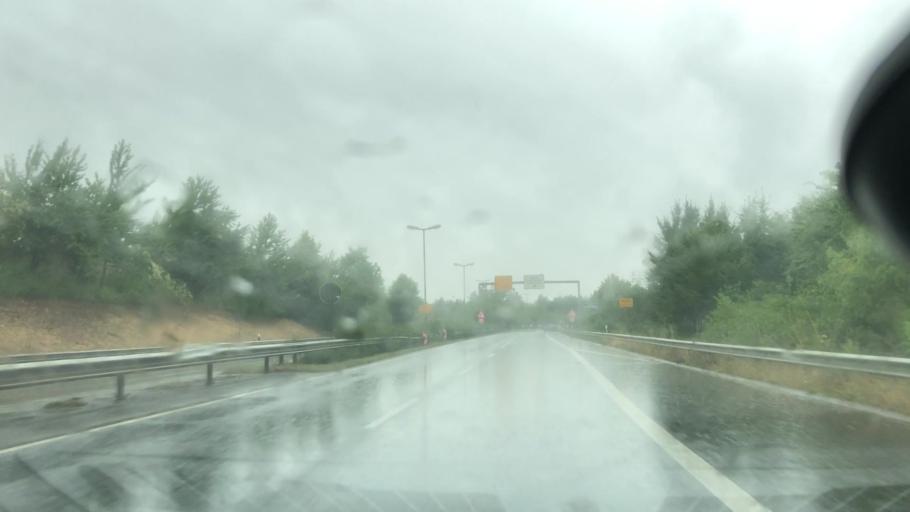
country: DE
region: North Rhine-Westphalia
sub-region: Regierungsbezirk Detmold
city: Minden
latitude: 52.2747
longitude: 8.9058
